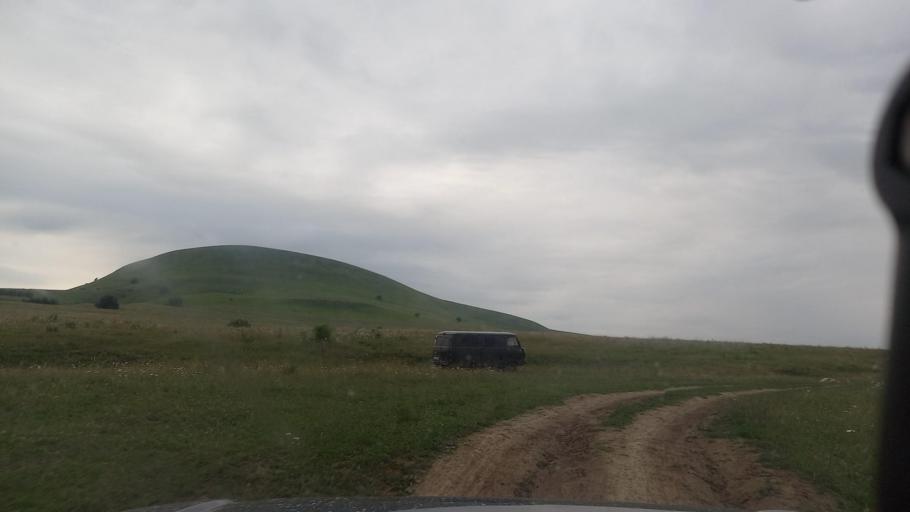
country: RU
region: Karachayevo-Cherkesiya
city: Pregradnaya
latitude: 43.9462
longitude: 41.1588
